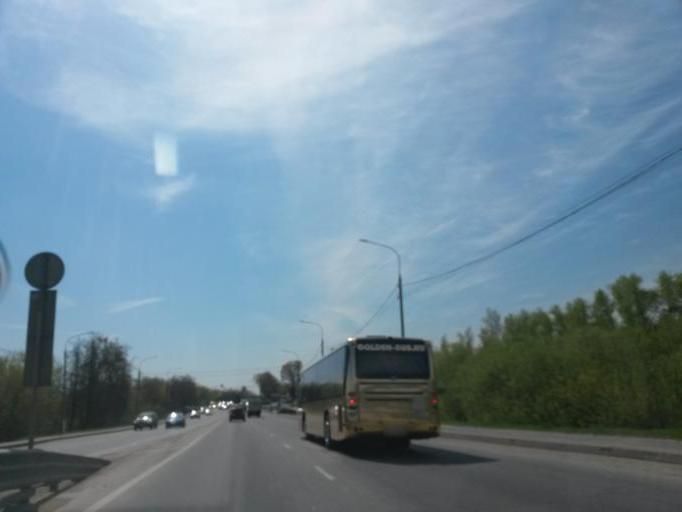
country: RU
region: Moskovskaya
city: Shcherbinka
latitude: 55.4625
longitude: 37.5596
